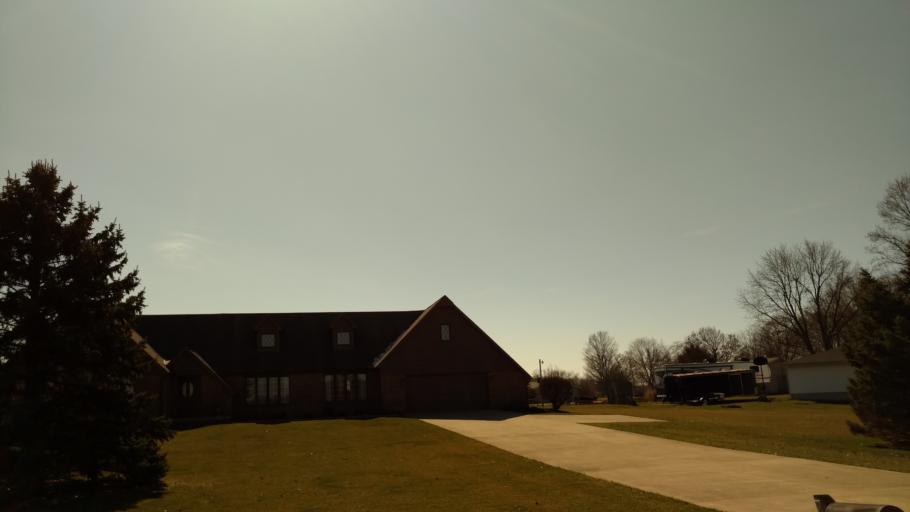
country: US
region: Ohio
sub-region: Marion County
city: Prospect
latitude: 40.4911
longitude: -83.1698
